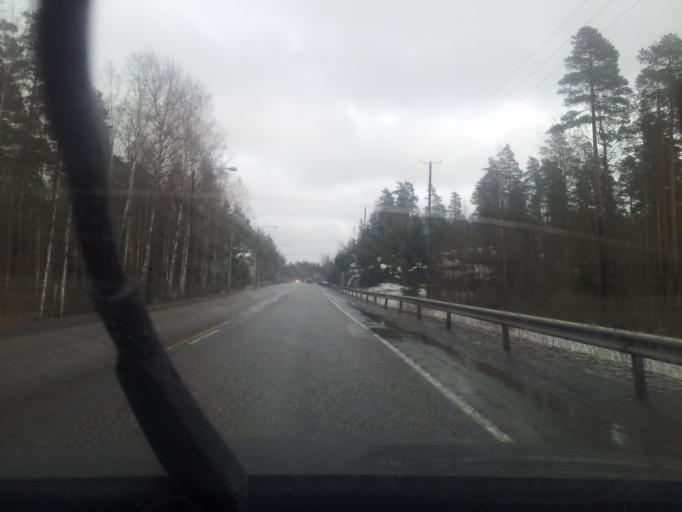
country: FI
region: Uusimaa
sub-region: Helsinki
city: Espoo
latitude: 60.2043
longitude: 24.6155
